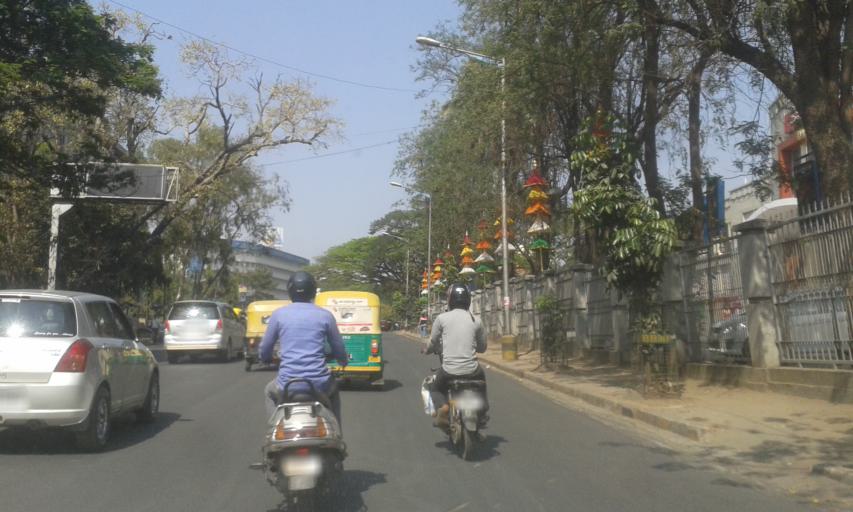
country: IN
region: Karnataka
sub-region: Bangalore Urban
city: Bangalore
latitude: 12.9621
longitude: 77.5845
